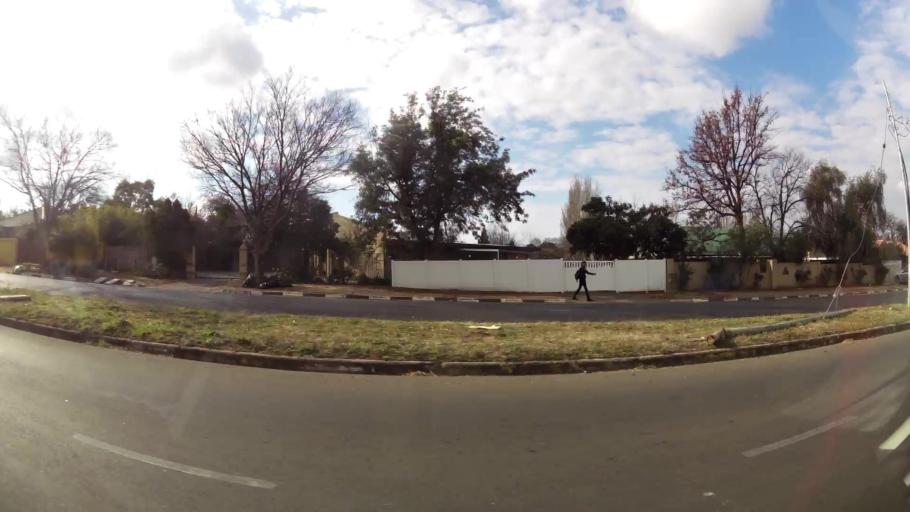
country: ZA
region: Orange Free State
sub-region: Mangaung Metropolitan Municipality
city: Bloemfontein
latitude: -29.0804
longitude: 26.2107
